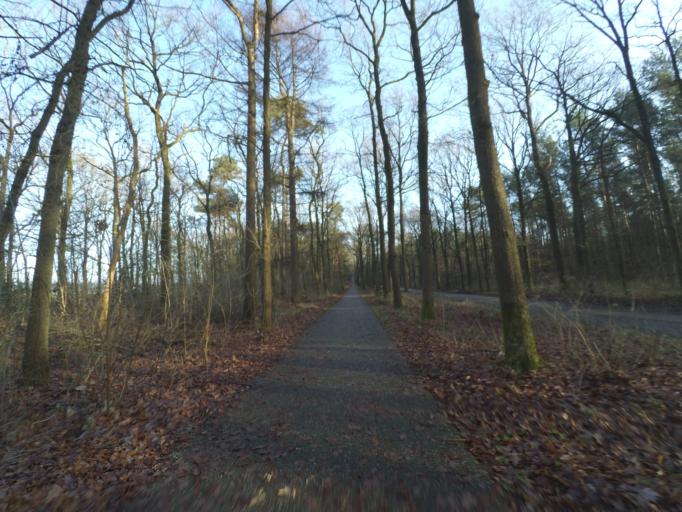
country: NL
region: Drenthe
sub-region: Gemeente Borger-Odoorn
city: Borger
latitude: 52.8732
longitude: 6.7884
